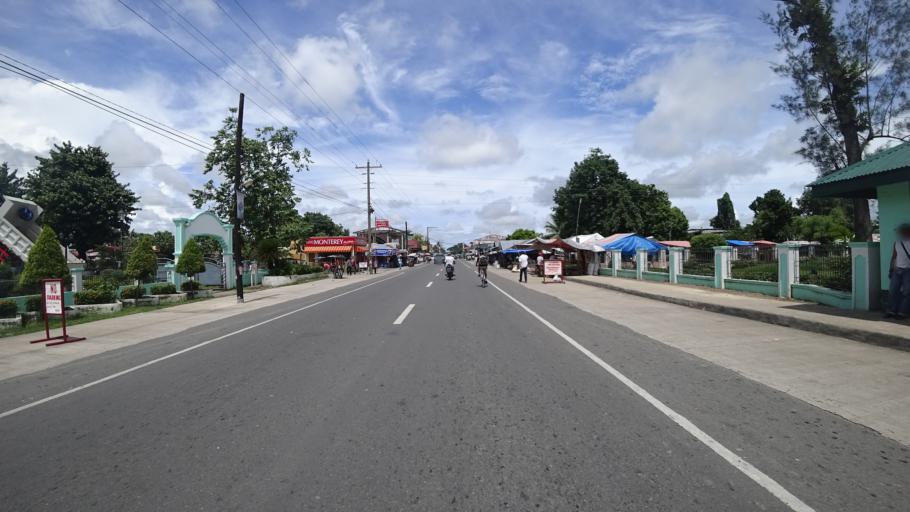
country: PH
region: Eastern Visayas
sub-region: Province of Leyte
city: Alangalang
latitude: 11.2068
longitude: 124.8467
